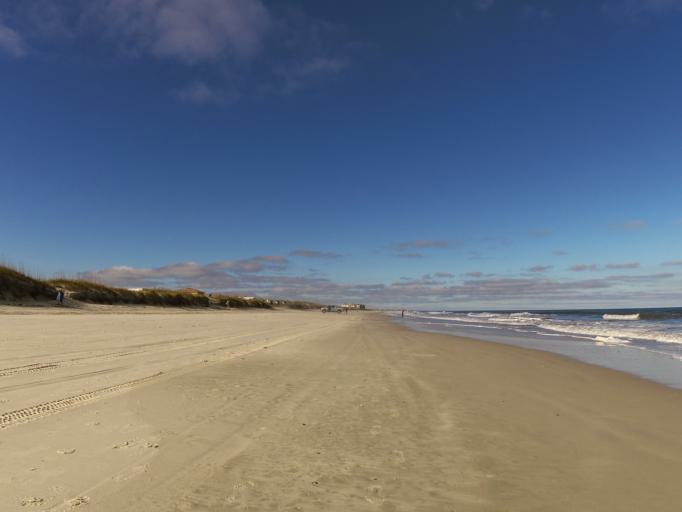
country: US
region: Florida
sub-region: Nassau County
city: Fernandina Beach
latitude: 30.5721
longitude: -81.4430
